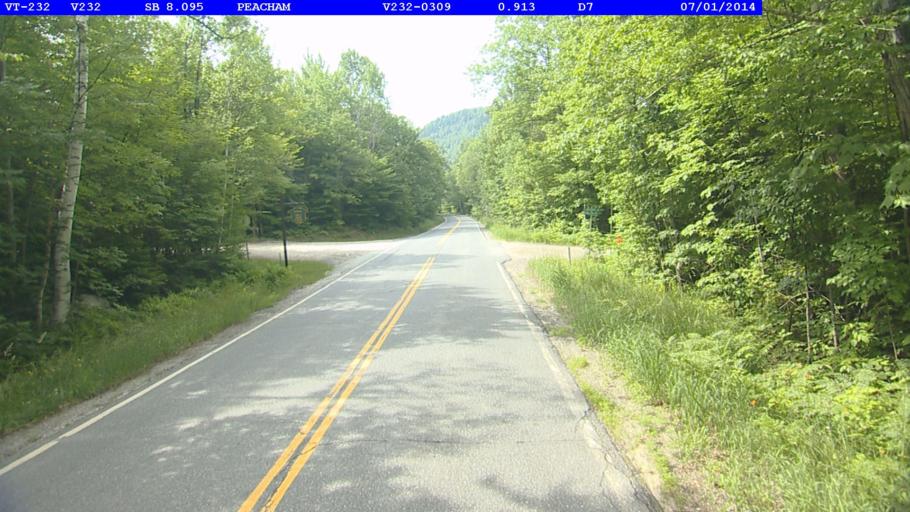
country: US
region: Vermont
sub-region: Caledonia County
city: Hardwick
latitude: 44.3085
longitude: -72.3029
